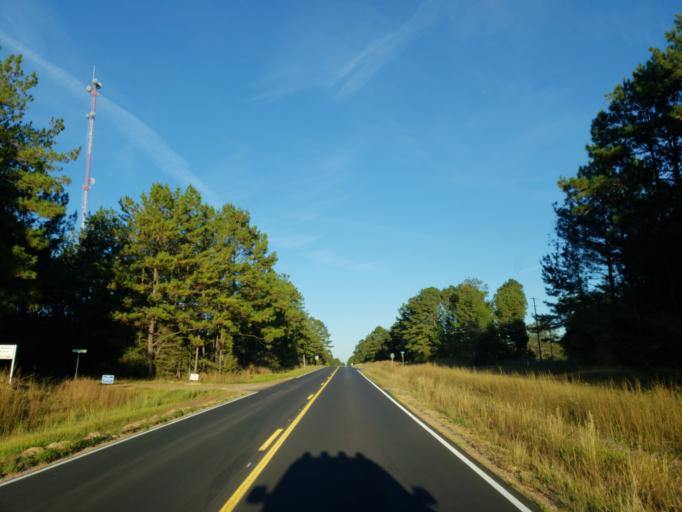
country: US
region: Mississippi
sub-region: Wayne County
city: Belmont
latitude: 31.4145
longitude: -88.5917
